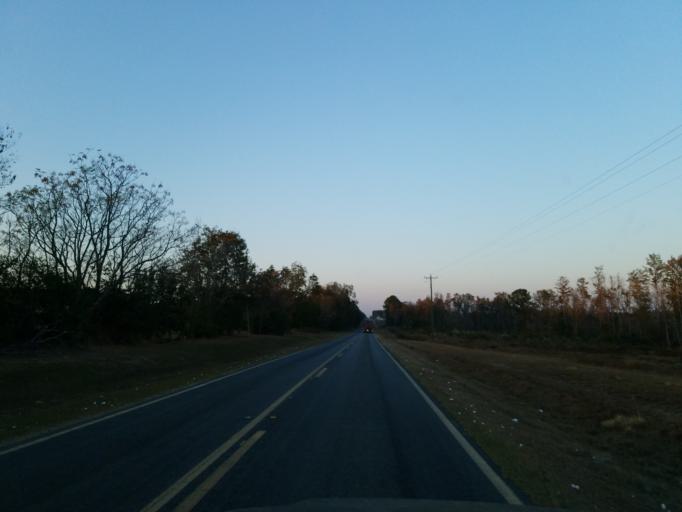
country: US
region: Georgia
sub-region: Ben Hill County
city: Fitzgerald
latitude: 31.7112
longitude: -83.3850
